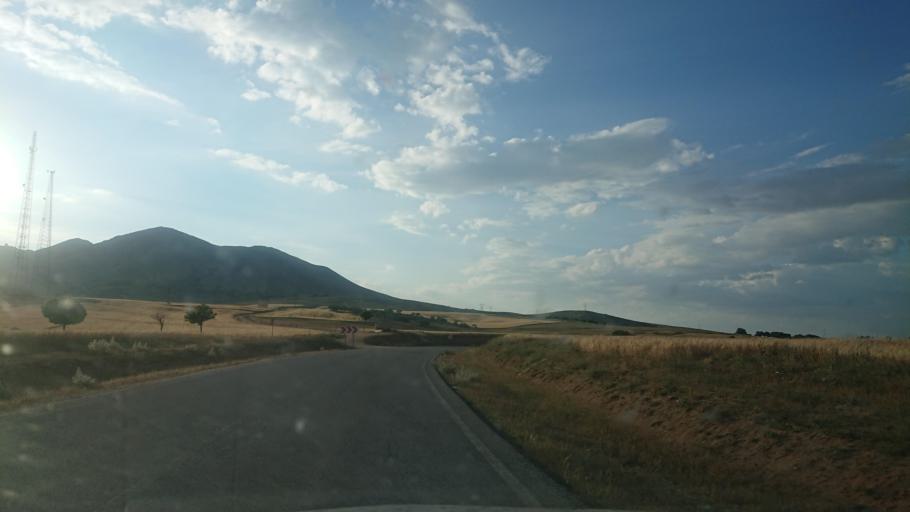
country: TR
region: Aksaray
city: Balci
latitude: 38.6193
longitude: 34.0962
